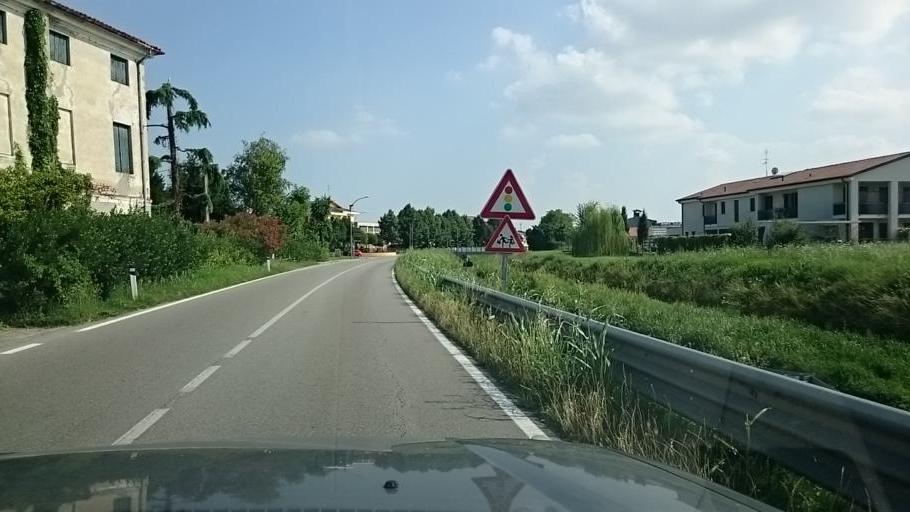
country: IT
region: Veneto
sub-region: Provincia di Padova
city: San Giorgio delle Pertiche
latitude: 45.5451
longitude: 11.8750
